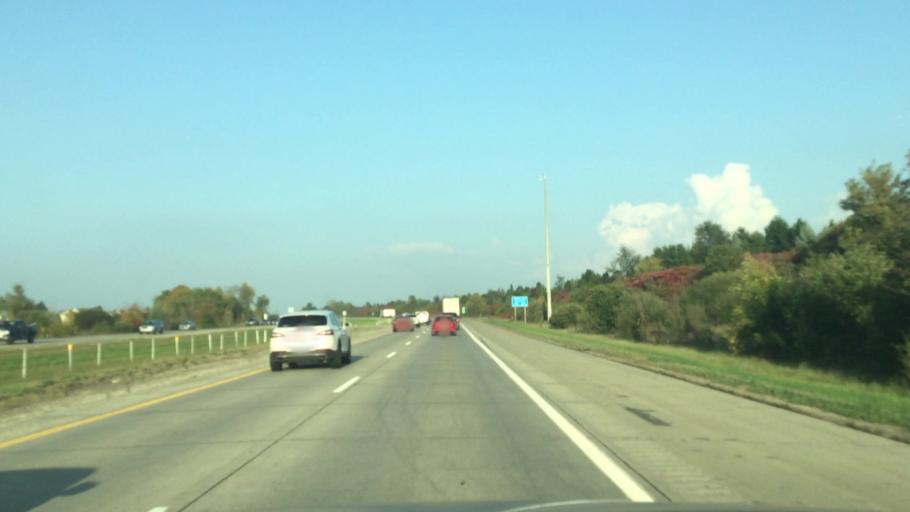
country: US
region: Michigan
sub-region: Wayne County
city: Plymouth
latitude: 42.3674
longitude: -83.5476
